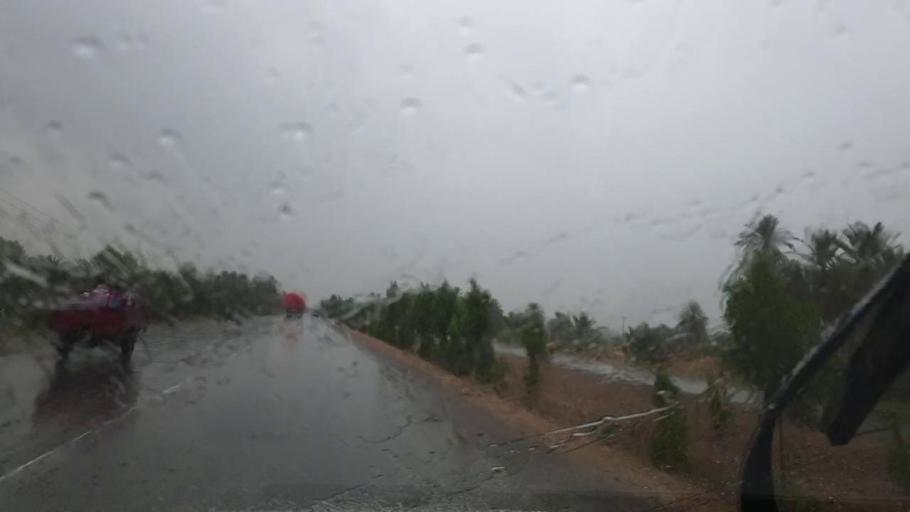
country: PK
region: Sindh
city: Khairpur
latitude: 27.5503
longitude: 68.7321
